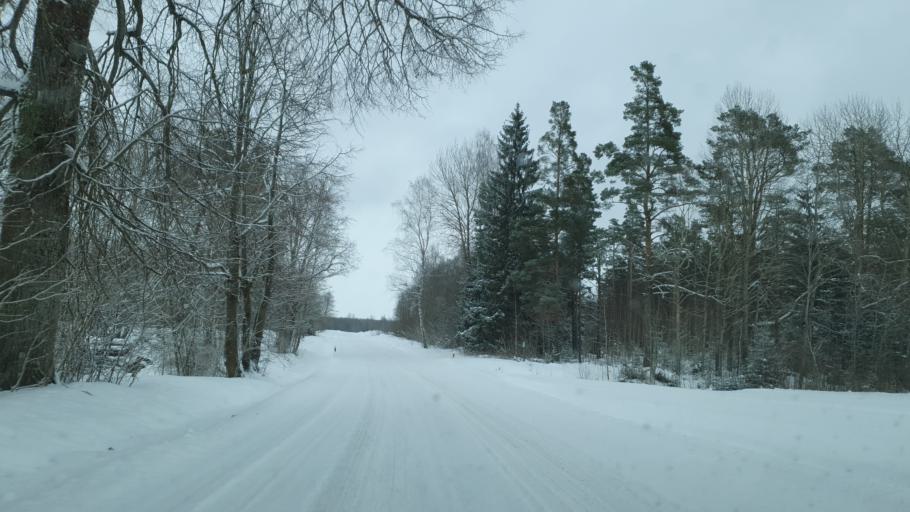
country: EE
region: Polvamaa
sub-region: Raepina vald
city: Rapina
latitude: 58.2041
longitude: 27.2956
